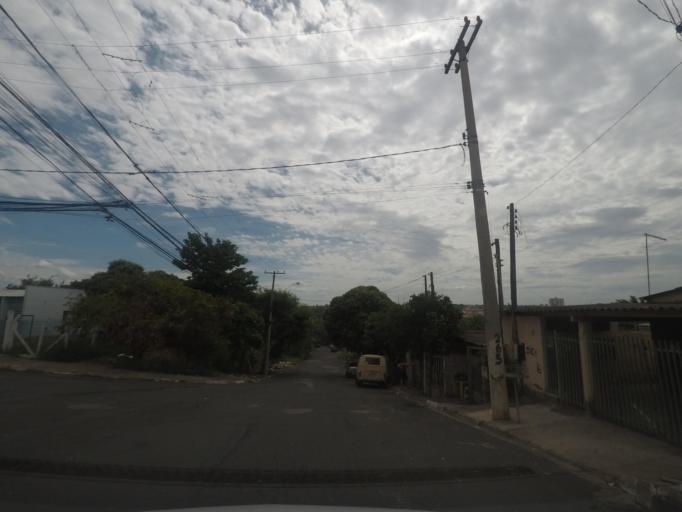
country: BR
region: Sao Paulo
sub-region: Sumare
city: Sumare
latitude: -22.8011
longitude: -47.2789
